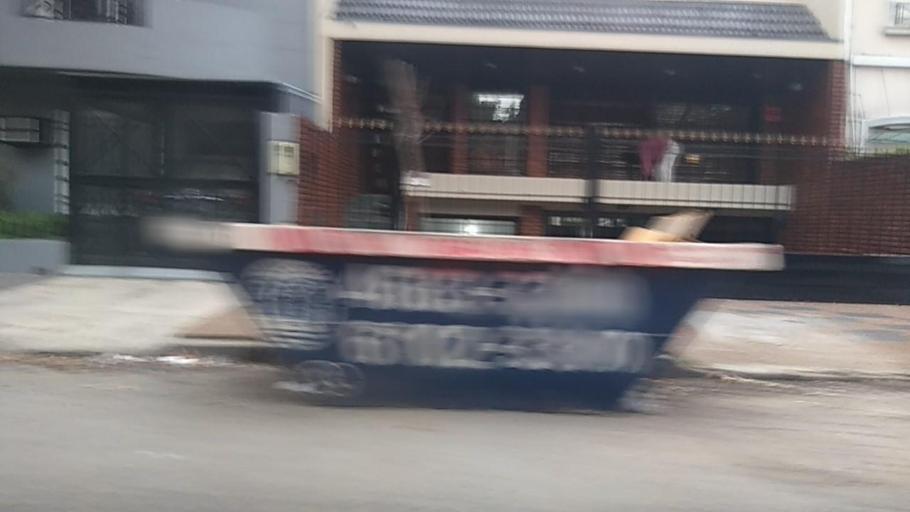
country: AR
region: Buenos Aires F.D.
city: Villa Santa Rita
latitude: -34.6010
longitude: -58.4992
